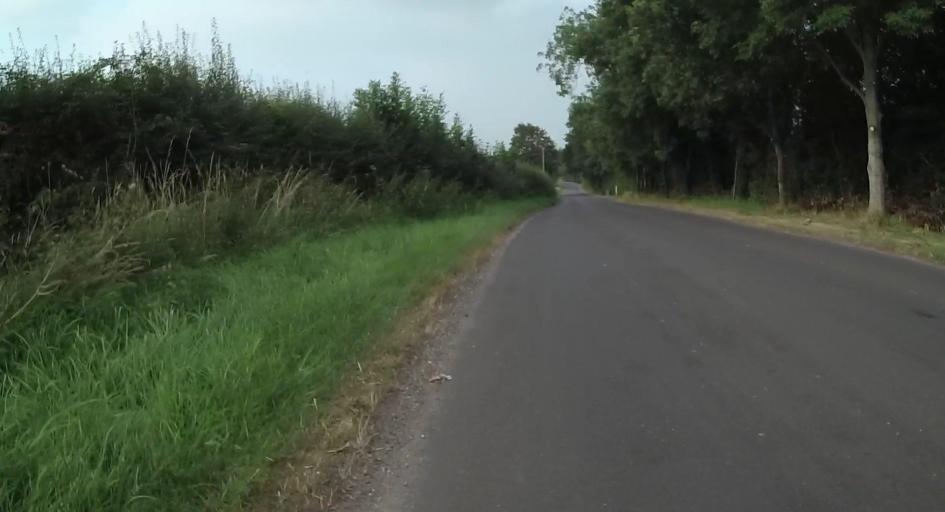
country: GB
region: England
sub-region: Hampshire
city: Old Basing
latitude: 51.2563
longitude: -1.0425
